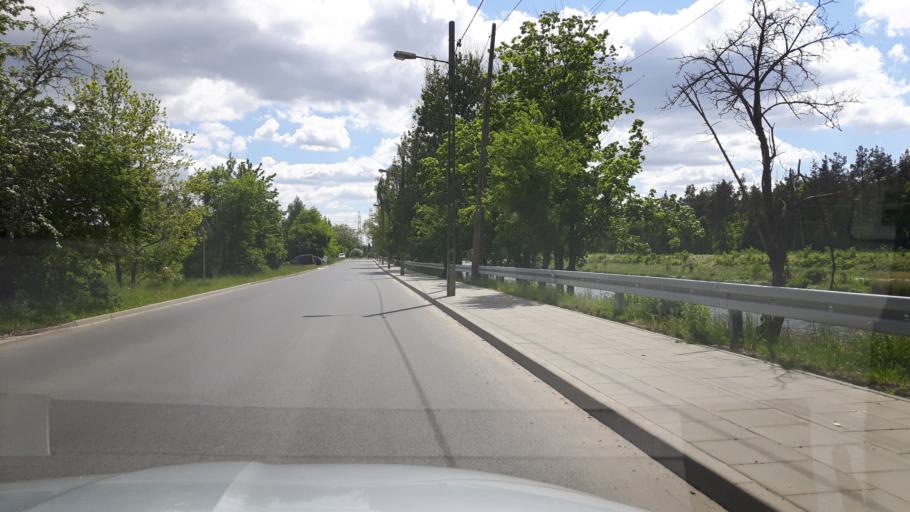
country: PL
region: Masovian Voivodeship
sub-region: Powiat legionowski
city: Stanislawow Pierwszy
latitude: 52.3344
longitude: 21.0329
